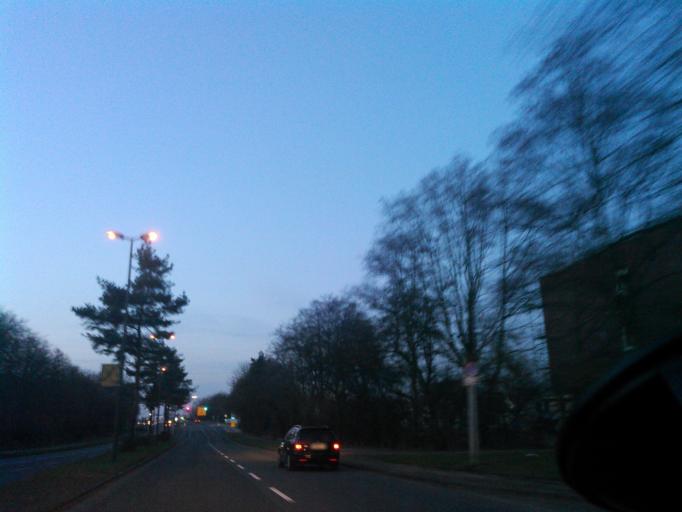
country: DE
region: North Rhine-Westphalia
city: Marl
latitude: 51.6534
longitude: 7.1038
